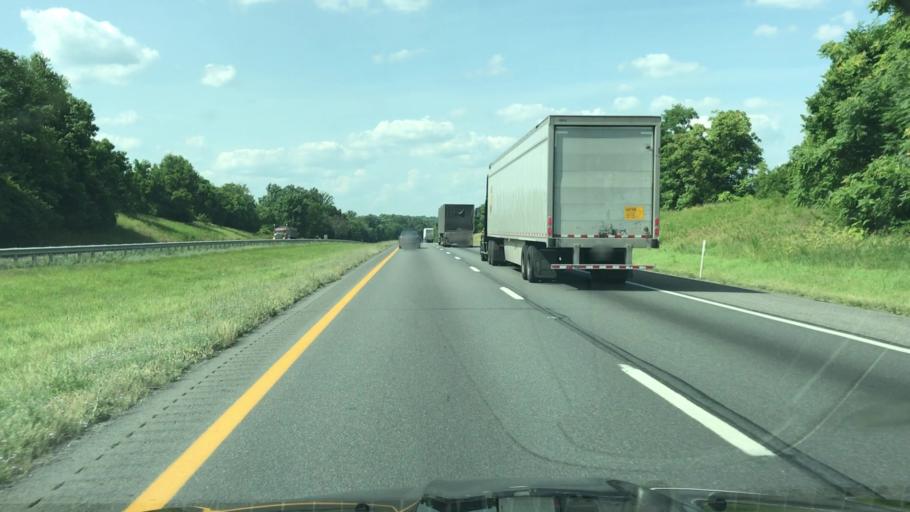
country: US
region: West Virginia
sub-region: Berkeley County
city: Inwood
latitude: 39.3940
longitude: -78.0277
